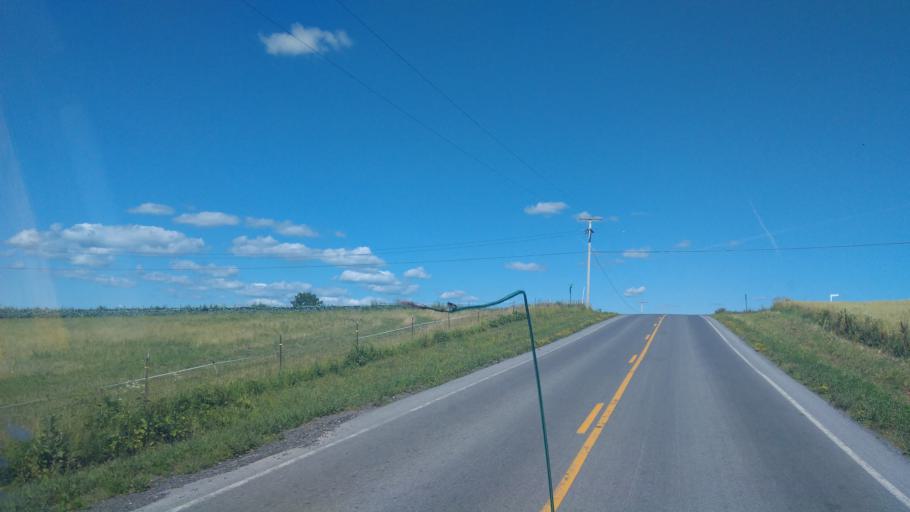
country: US
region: New York
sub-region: Wayne County
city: Clyde
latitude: 43.0251
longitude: -76.9211
